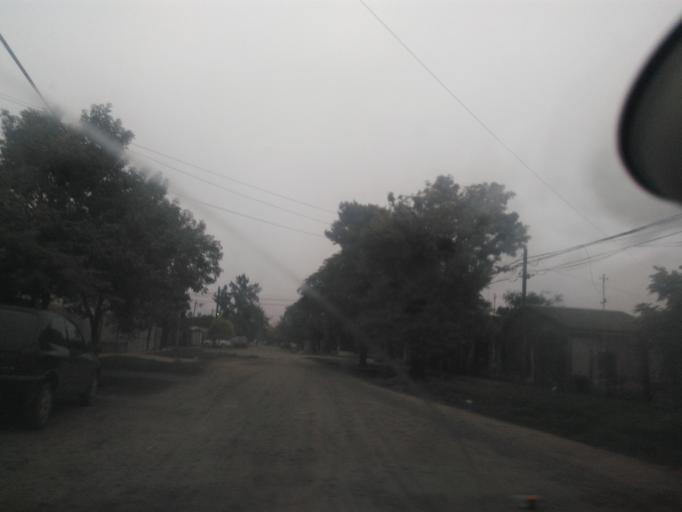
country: AR
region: Chaco
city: Resistencia
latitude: -27.4690
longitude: -58.9960
